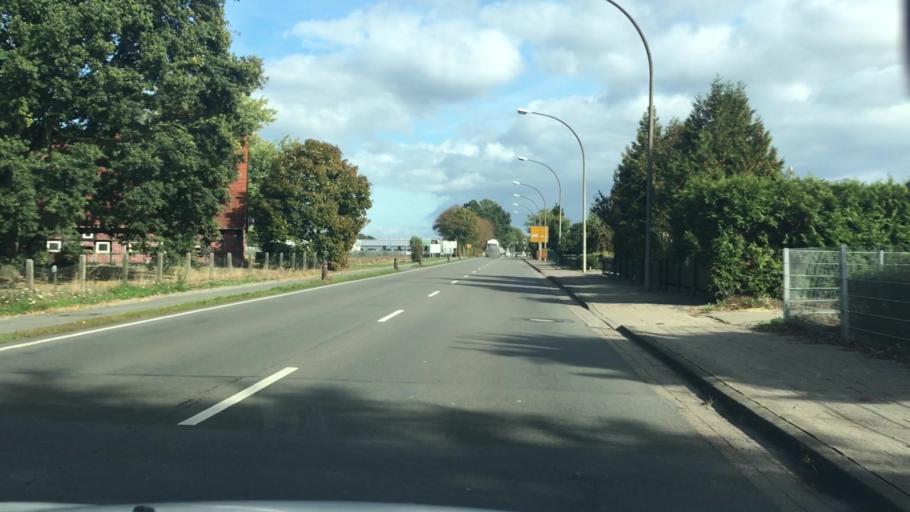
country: DE
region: Lower Saxony
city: Rehden
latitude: 52.6095
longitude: 8.4873
